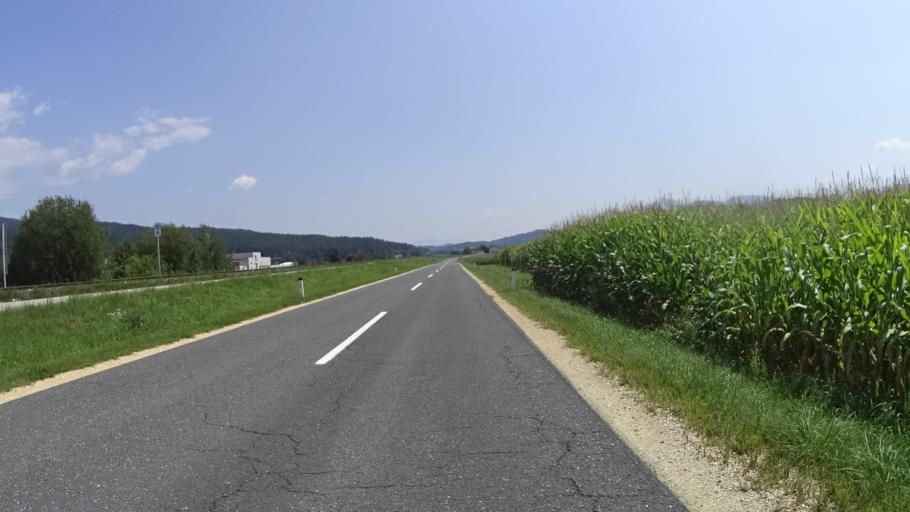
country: AT
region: Carinthia
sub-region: Politischer Bezirk Volkermarkt
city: Bleiburg/Pliberk
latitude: 46.5718
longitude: 14.7986
